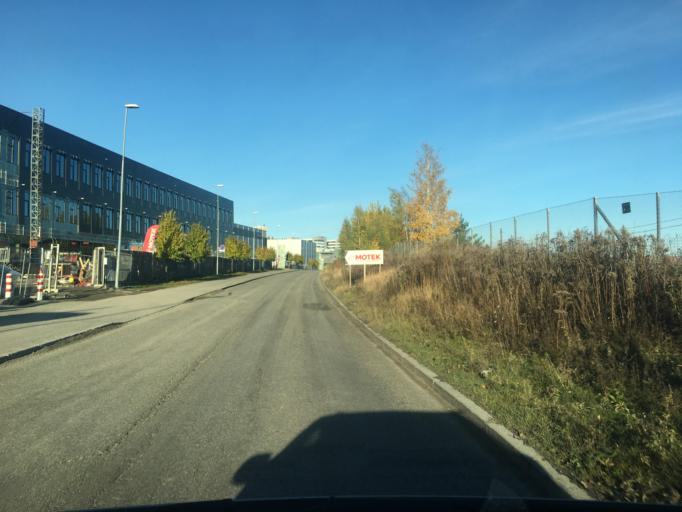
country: NO
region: Oslo
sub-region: Oslo
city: Oslo
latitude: 59.9332
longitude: 10.8352
